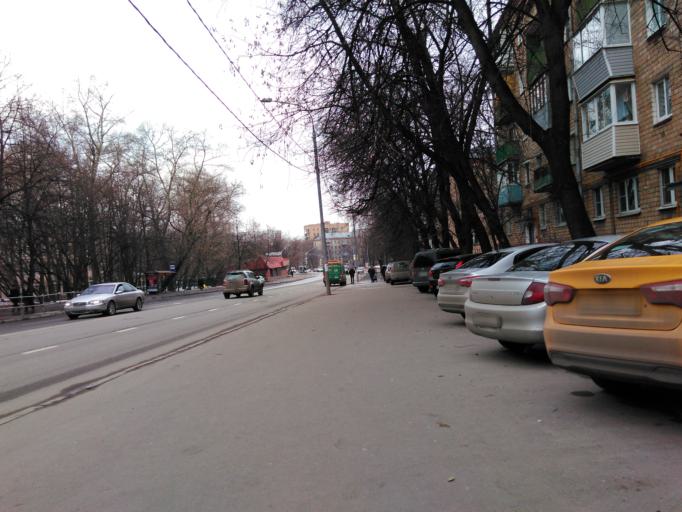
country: RU
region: Moscow
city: Vatutino
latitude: 55.8666
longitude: 37.6791
